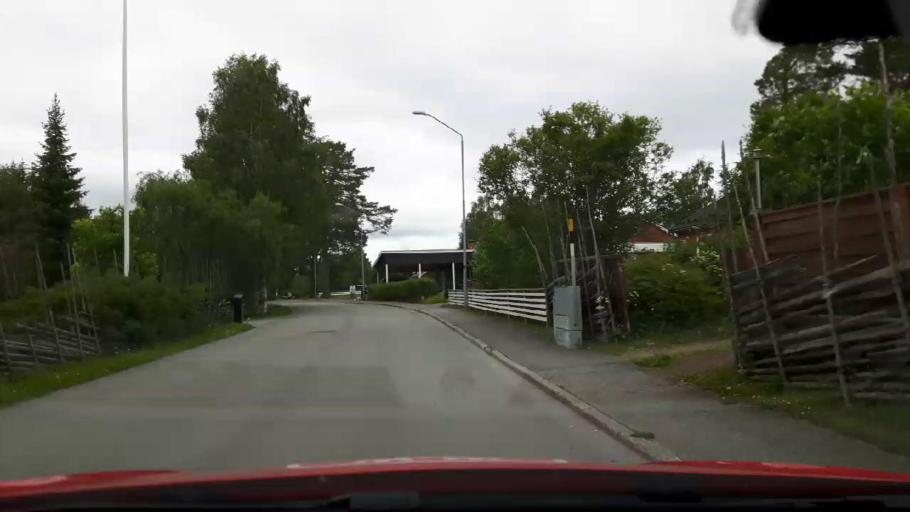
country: SE
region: Jaemtland
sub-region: OEstersunds Kommun
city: Ostersund
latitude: 63.2069
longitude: 14.6229
